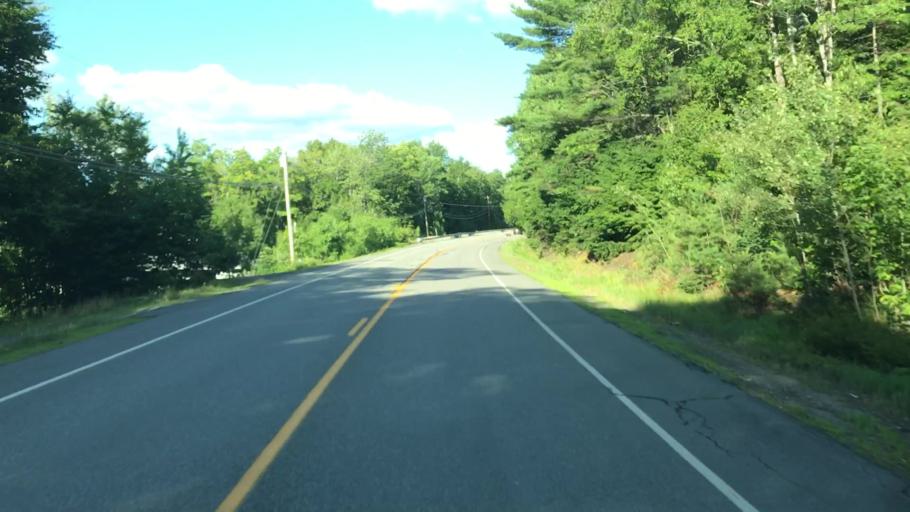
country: US
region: Maine
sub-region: Penobscot County
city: Lincoln
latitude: 45.3787
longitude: -68.4532
